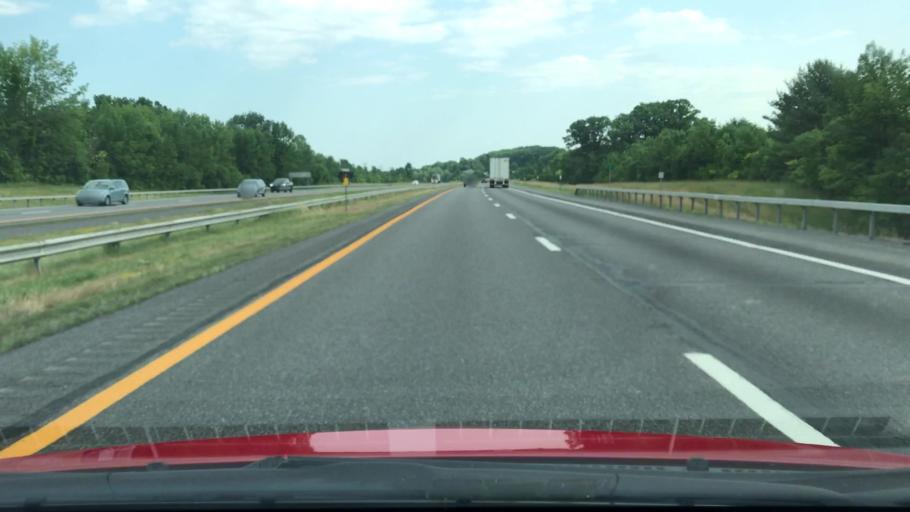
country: US
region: New York
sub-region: Albany County
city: Ravena
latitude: 42.4612
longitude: -73.8081
